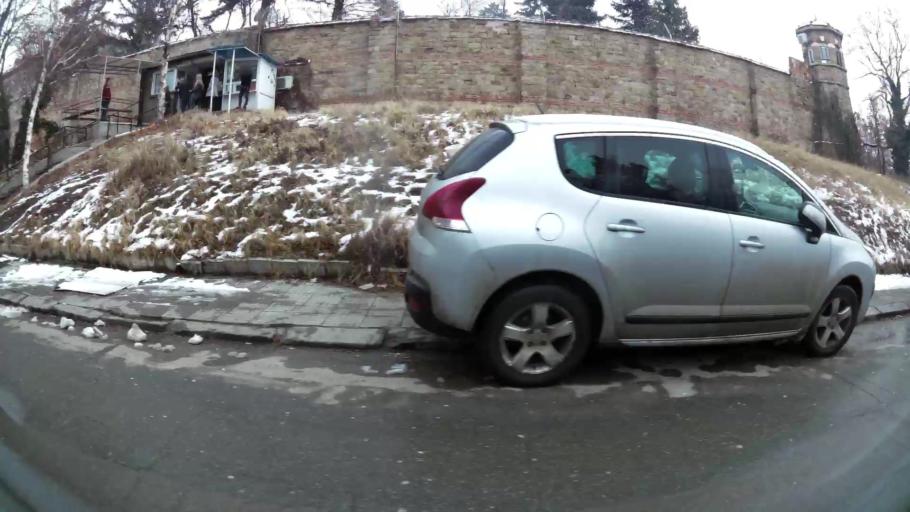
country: BG
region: Sofia-Capital
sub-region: Stolichna Obshtina
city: Sofia
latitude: 42.7081
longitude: 23.3028
